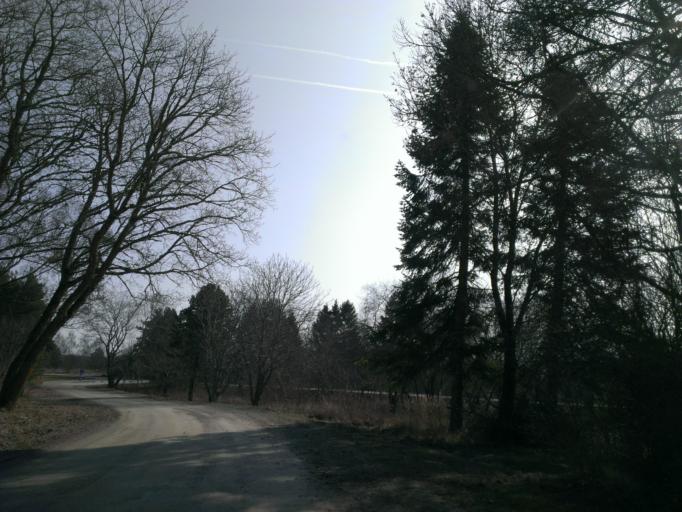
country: EE
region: Saare
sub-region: Orissaare vald
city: Orissaare
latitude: 58.5587
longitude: 23.0883
